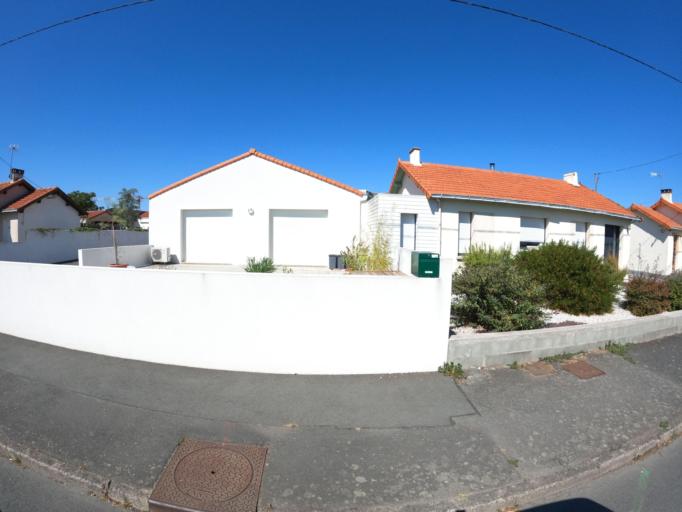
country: FR
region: Pays de la Loire
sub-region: Departement de la Vendee
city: Montaigu
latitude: 46.9691
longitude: -1.3049
